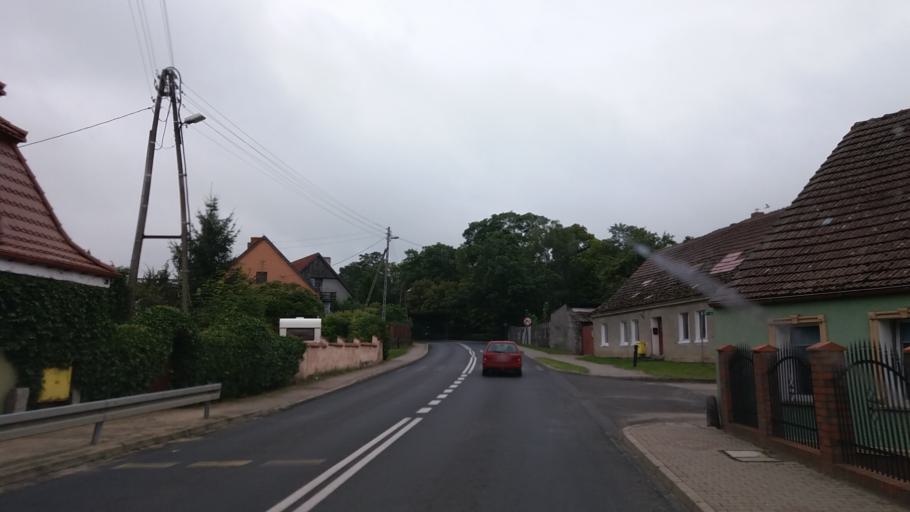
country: PL
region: West Pomeranian Voivodeship
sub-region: Powiat choszczenski
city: Pelczyce
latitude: 53.0388
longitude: 15.3022
